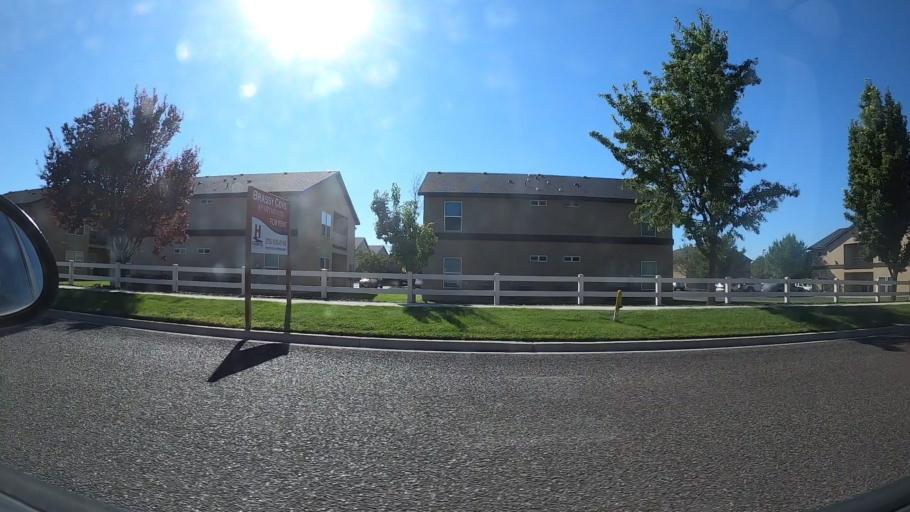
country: US
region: Idaho
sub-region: Canyon County
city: Nampa
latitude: 43.6009
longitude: -116.6132
